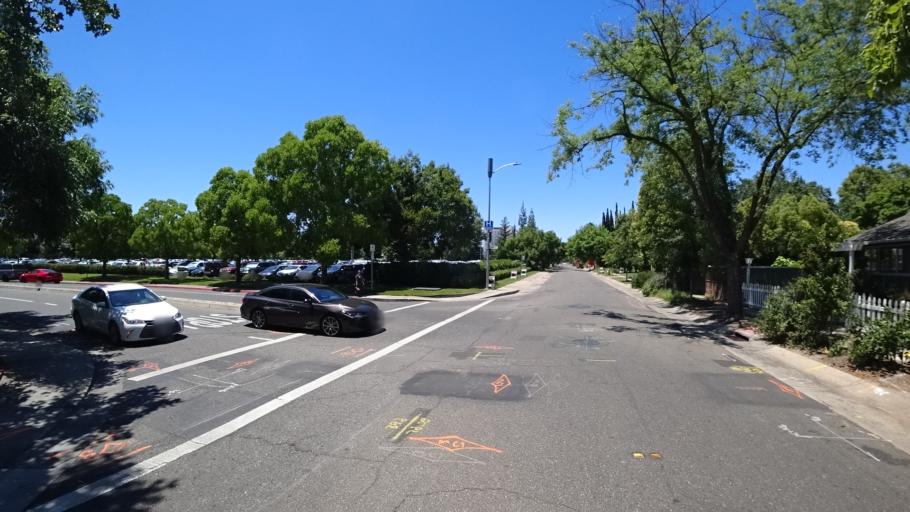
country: US
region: California
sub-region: Sacramento County
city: Sacramento
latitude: 38.5540
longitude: -121.4479
